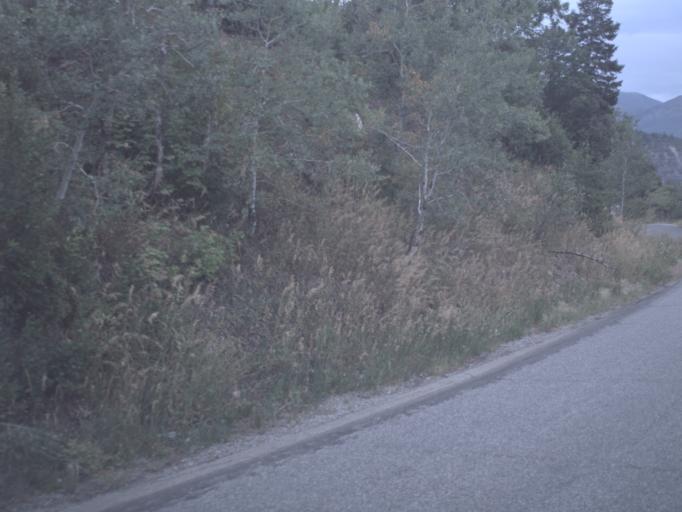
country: US
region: Utah
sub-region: Utah County
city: Lindon
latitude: 40.3995
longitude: -111.5940
